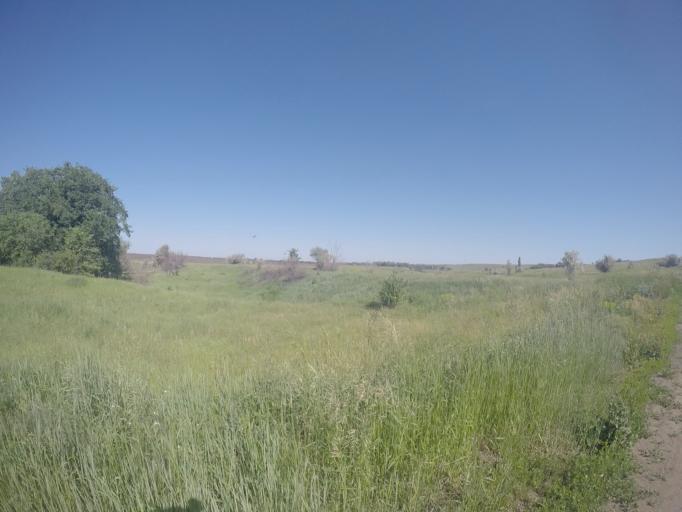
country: RU
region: Saratov
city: Krasnoarmeysk
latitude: 51.2637
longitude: 45.5971
